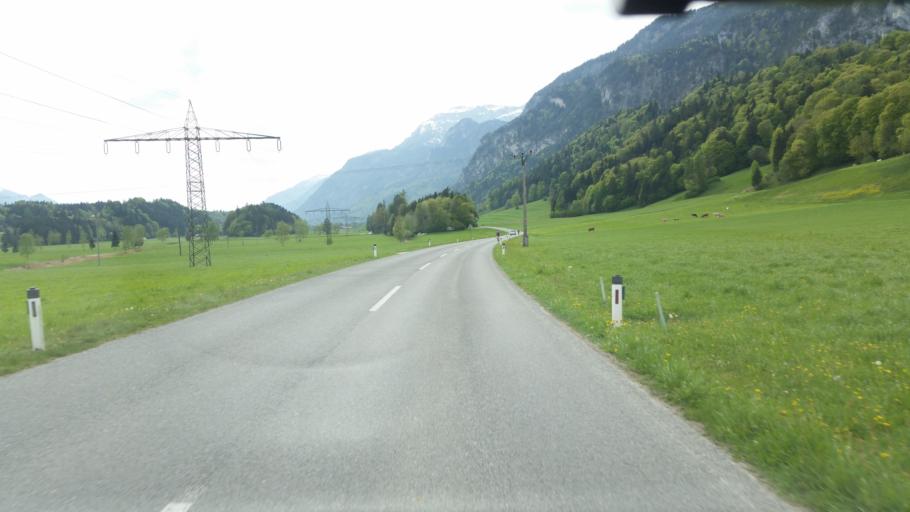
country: AT
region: Tyrol
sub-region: Politischer Bezirk Kufstein
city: Radfeld
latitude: 47.4721
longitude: 11.9311
